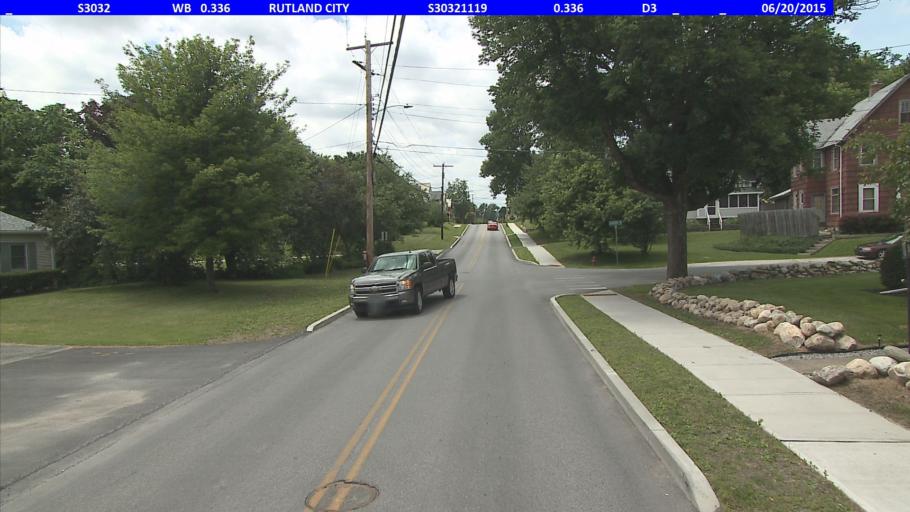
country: US
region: Vermont
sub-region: Rutland County
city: Rutland
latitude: 43.6056
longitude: -72.9652
